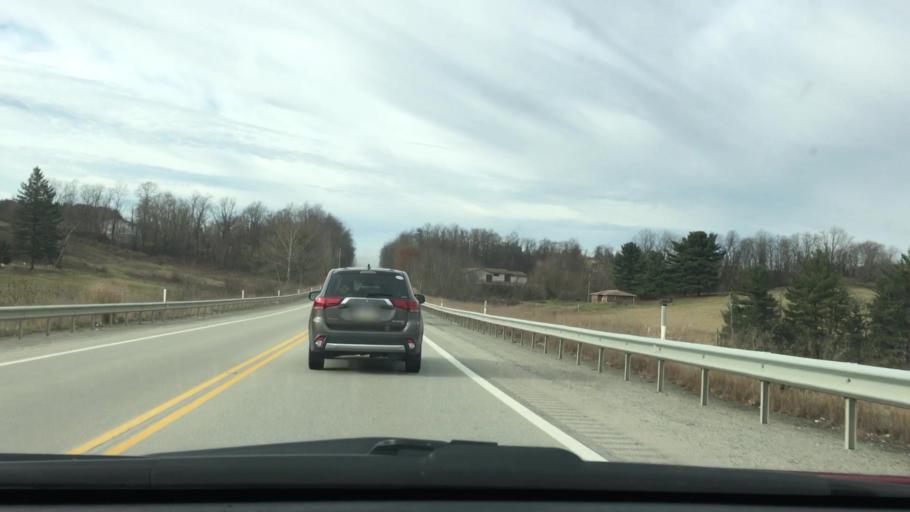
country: US
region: Pennsylvania
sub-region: Fayette County
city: South Uniontown
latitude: 39.8927
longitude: -79.8298
